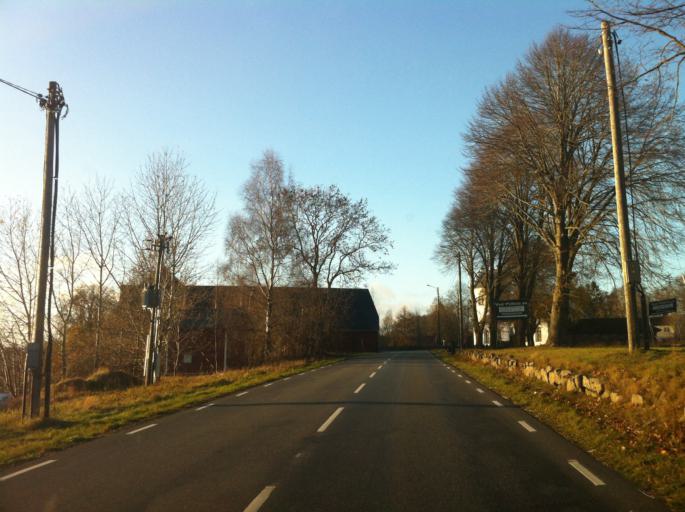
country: SE
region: Skane
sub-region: Ostra Goinge Kommun
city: Knislinge
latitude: 56.1855
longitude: 14.0003
